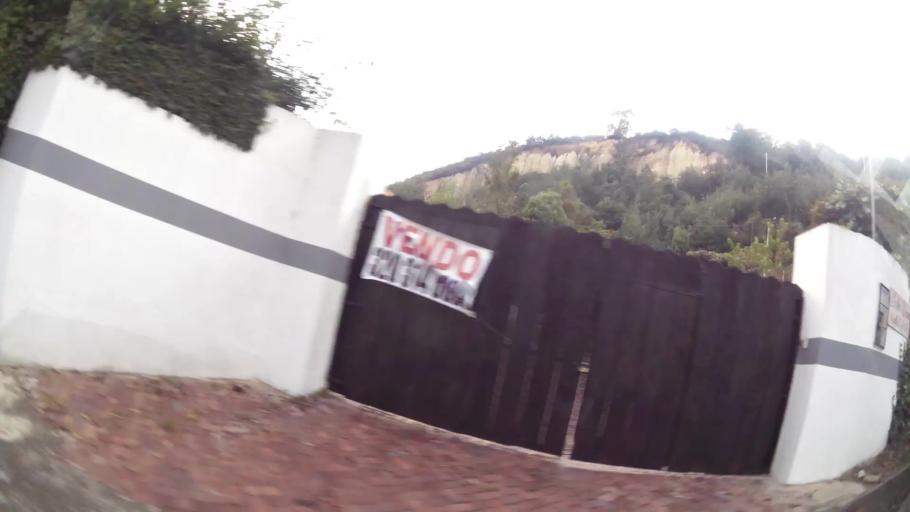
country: CO
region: Cundinamarca
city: Cota
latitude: 4.8131
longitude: -74.1074
